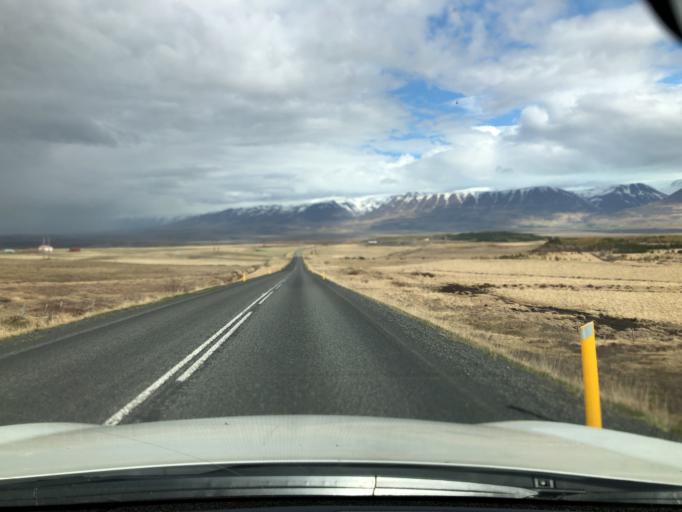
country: IS
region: Northwest
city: Saudarkrokur
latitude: 65.5419
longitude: -19.5004
